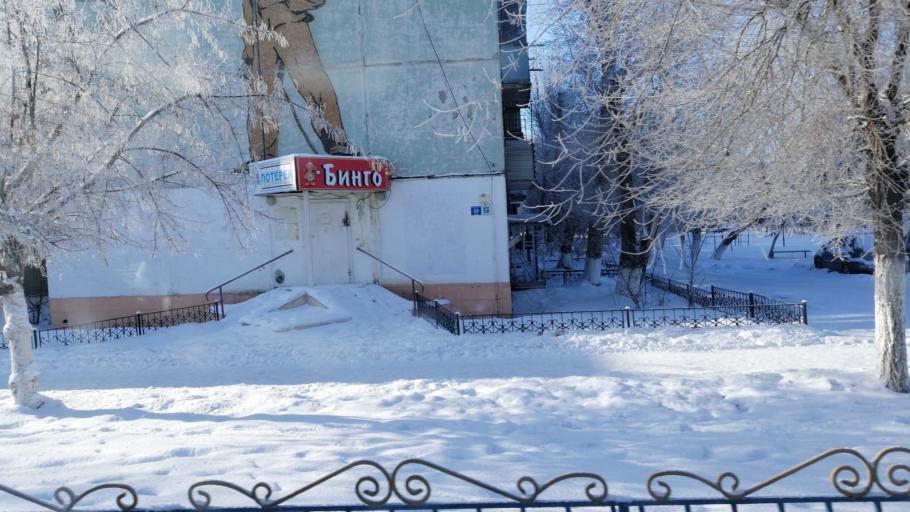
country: KZ
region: Aqtoebe
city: Aqtobe
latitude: 50.3051
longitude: 57.1509
